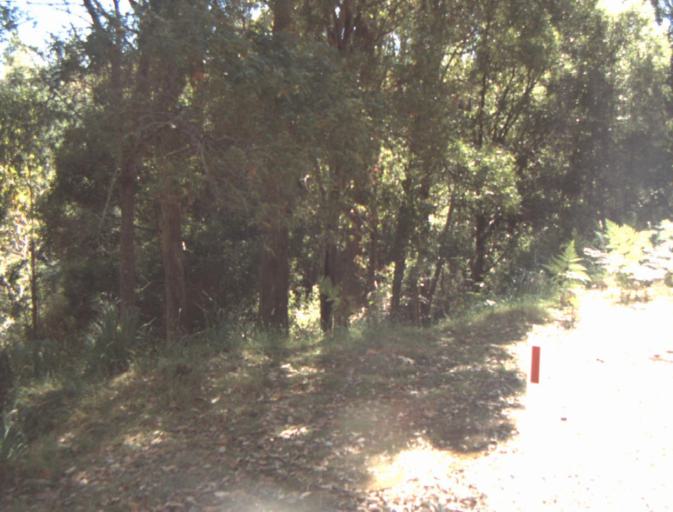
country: AU
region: Tasmania
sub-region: Launceston
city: Newstead
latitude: -41.3227
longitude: 147.3317
